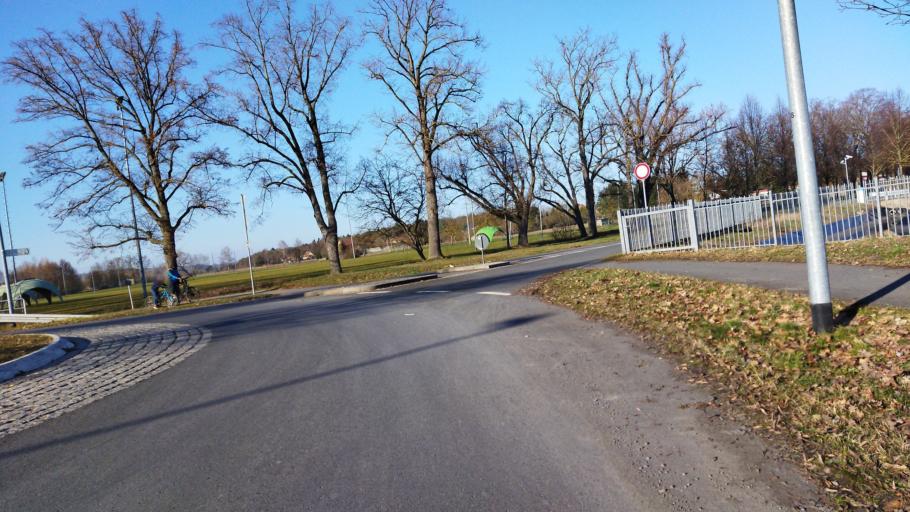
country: DE
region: Bavaria
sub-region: Regierungsbezirk Unterfranken
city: Kitzingen
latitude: 49.7463
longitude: 10.1628
